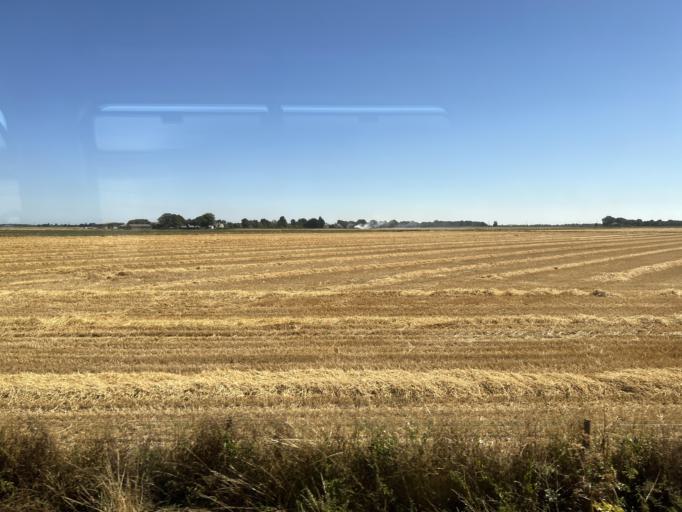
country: GB
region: England
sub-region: Lincolnshire
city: Spilsby
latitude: 53.0976
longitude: 0.1071
